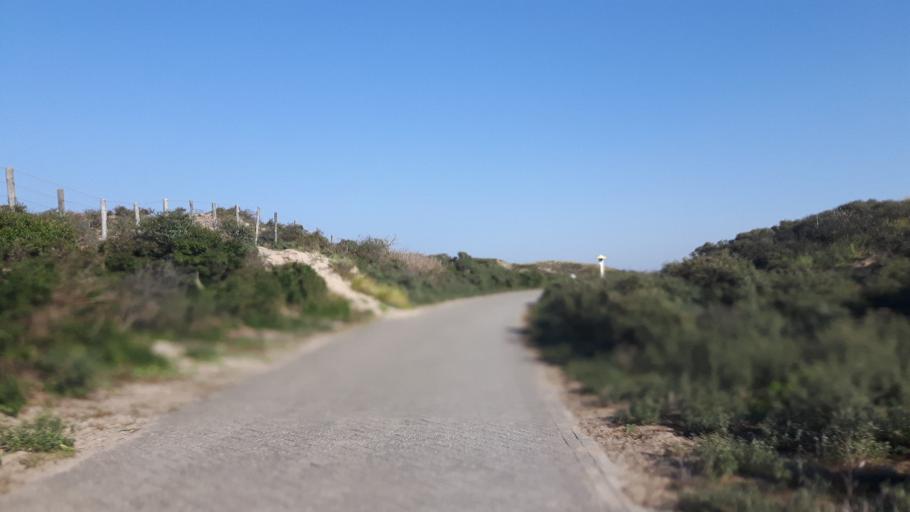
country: NL
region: South Holland
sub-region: Gemeente Noordwijkerhout
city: Noordwijkerhout
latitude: 52.2970
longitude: 4.4744
